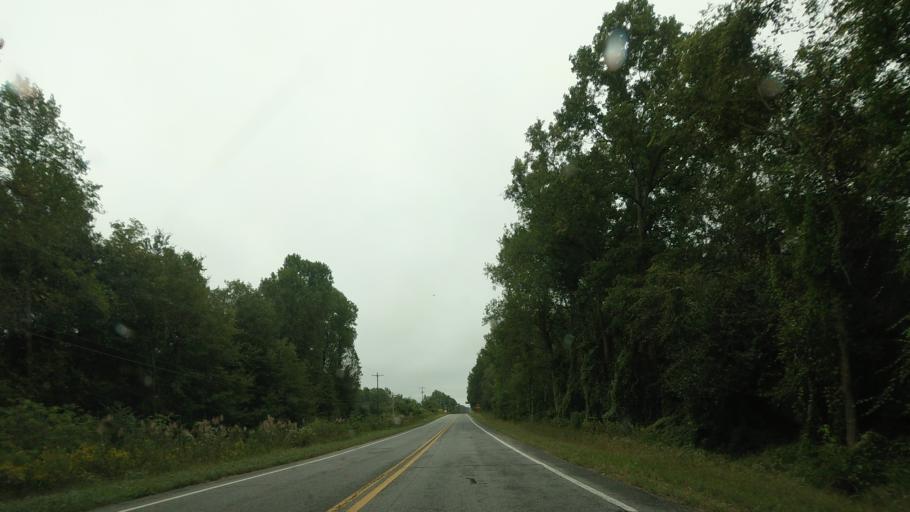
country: US
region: Georgia
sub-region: Irwin County
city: Ocilla
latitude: 31.4833
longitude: -83.2381
